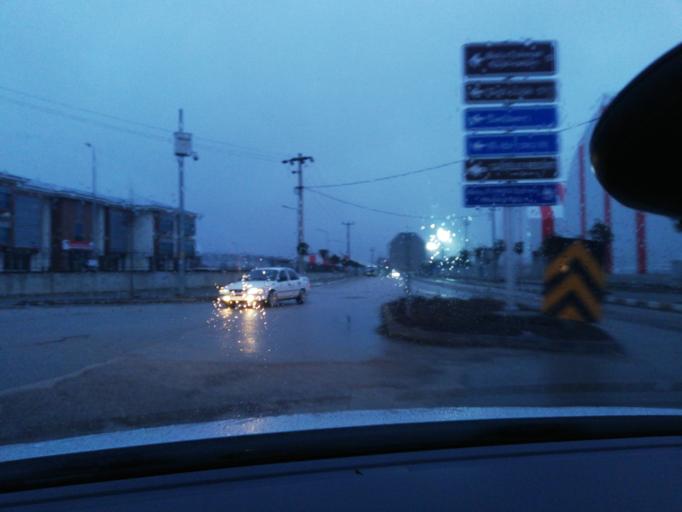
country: TR
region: Bolu
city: Bolu
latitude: 40.7233
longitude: 31.6088
